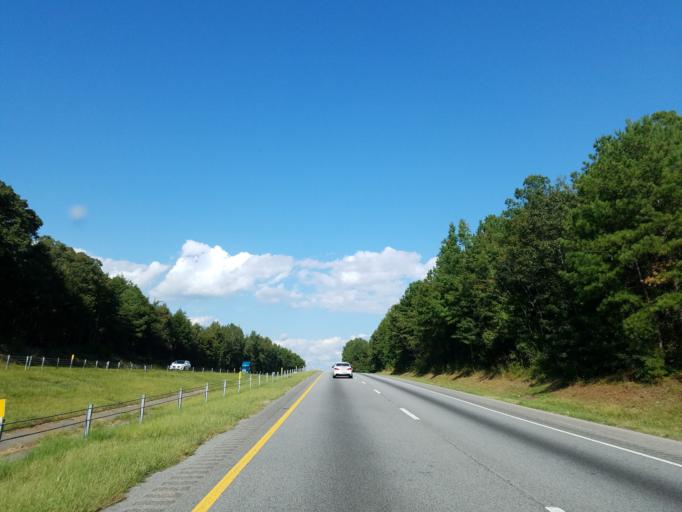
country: US
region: South Carolina
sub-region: Anderson County
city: Centerville
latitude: 34.5411
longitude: -82.8170
